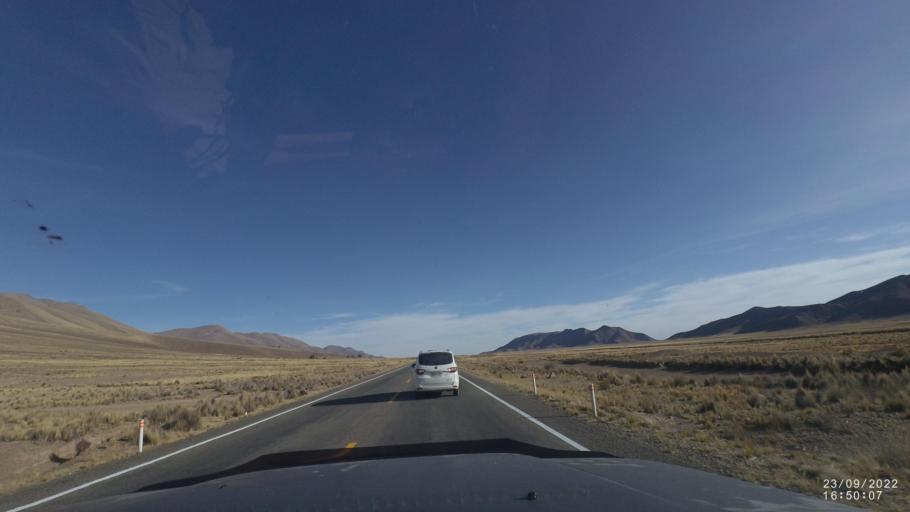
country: BO
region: Oruro
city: Poopo
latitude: -18.3985
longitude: -66.9777
